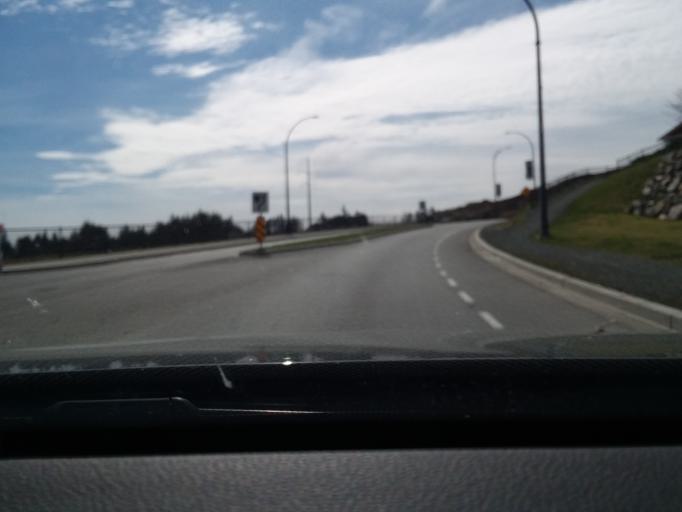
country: CA
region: British Columbia
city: Langford
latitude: 48.4515
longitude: -123.5414
